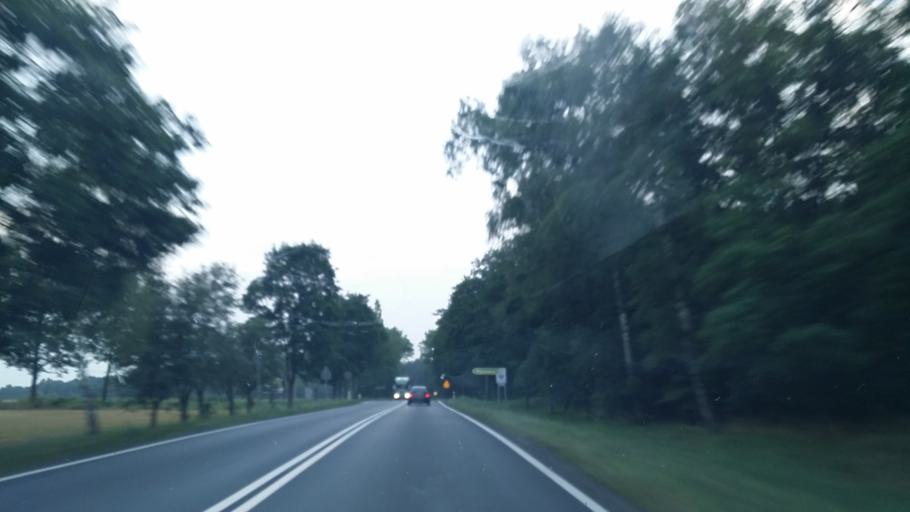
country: PL
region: Lower Silesian Voivodeship
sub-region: Powiat legnicki
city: Prochowice
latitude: 51.3036
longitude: 16.3344
